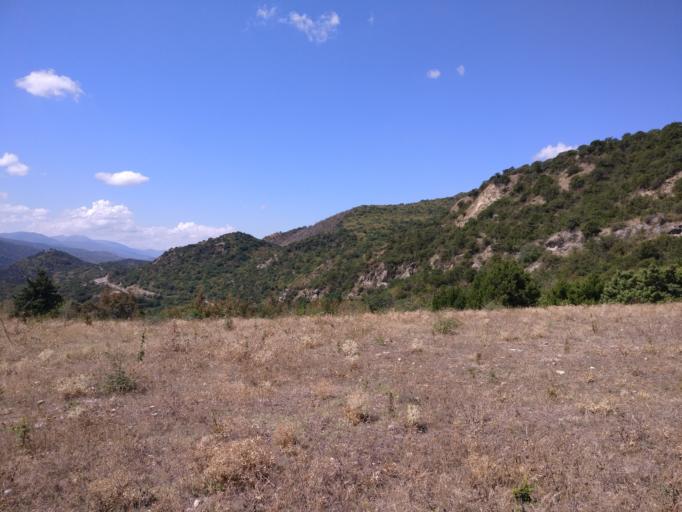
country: GE
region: Mtskheta-Mtianeti
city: Mtskheta
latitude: 41.8476
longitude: 44.6953
